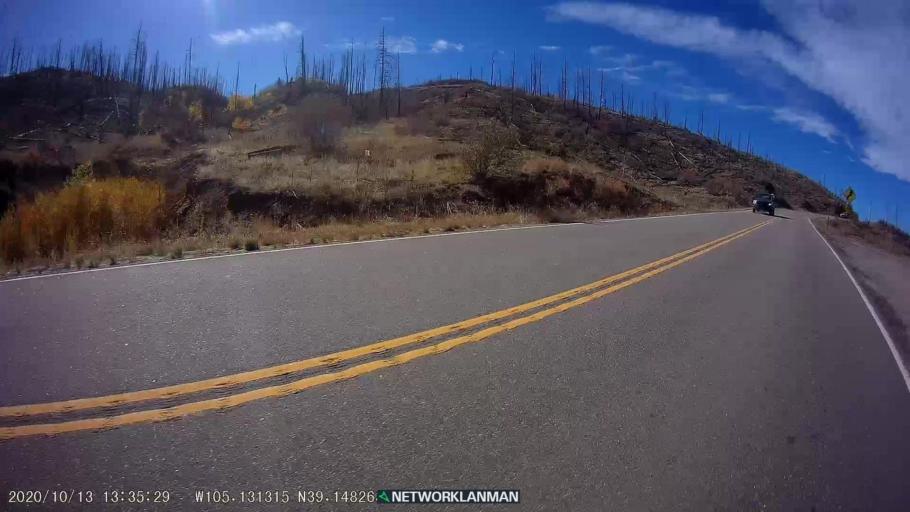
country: US
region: Colorado
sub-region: Teller County
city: Woodland Park
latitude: 39.1485
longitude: -105.1314
